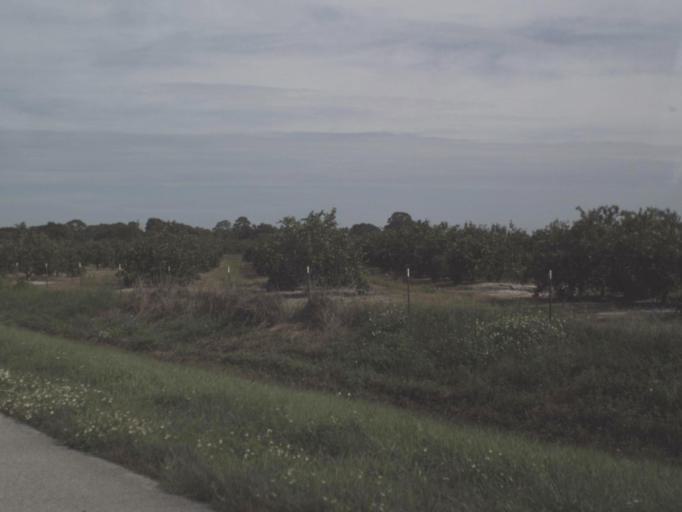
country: US
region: Florida
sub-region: DeSoto County
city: Nocatee
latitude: 27.0583
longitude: -81.7881
